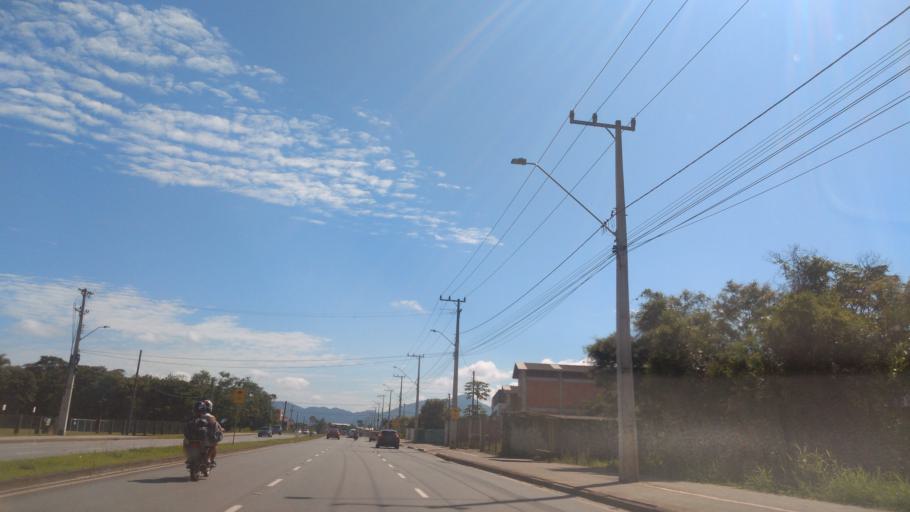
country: BR
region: Santa Catarina
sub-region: Joinville
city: Joinville
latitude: -26.2315
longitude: -48.8075
